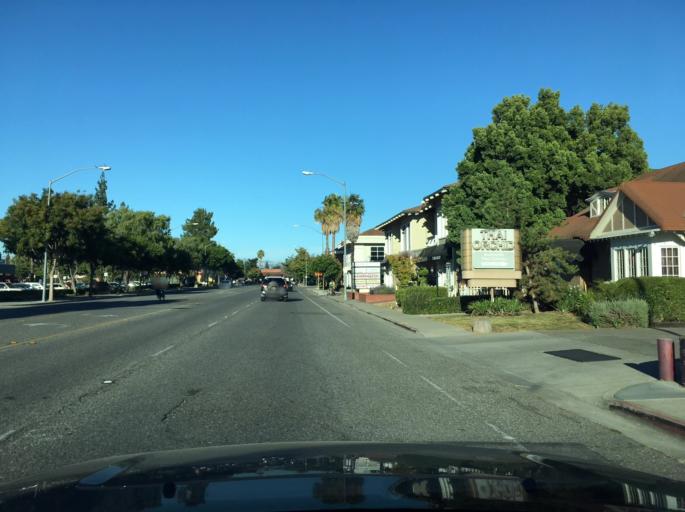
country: US
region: California
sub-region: Santa Clara County
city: Campbell
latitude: 37.2870
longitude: -121.9348
